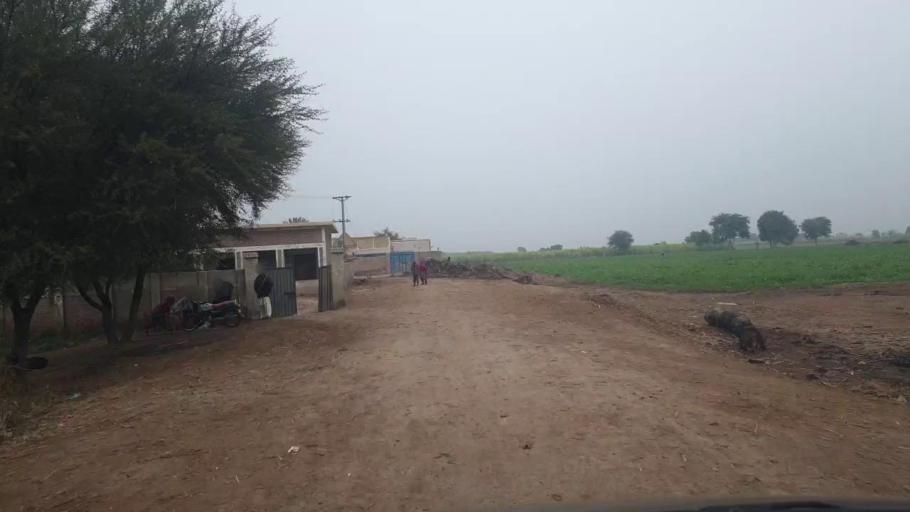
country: PK
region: Sindh
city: Tando Adam
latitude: 25.8039
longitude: 68.6875
